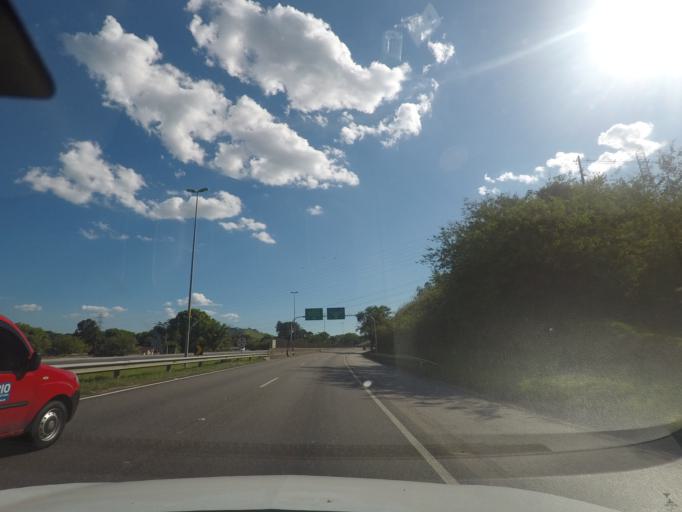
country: BR
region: Rio de Janeiro
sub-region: Guapimirim
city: Guapimirim
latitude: -22.6032
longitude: -43.0256
